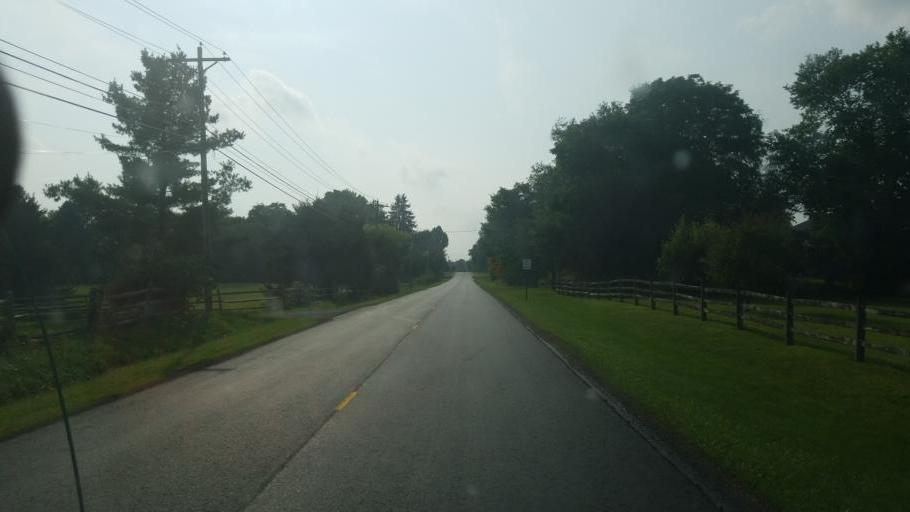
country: US
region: Ohio
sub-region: Medina County
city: Westfield Center
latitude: 41.0272
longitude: -81.9633
